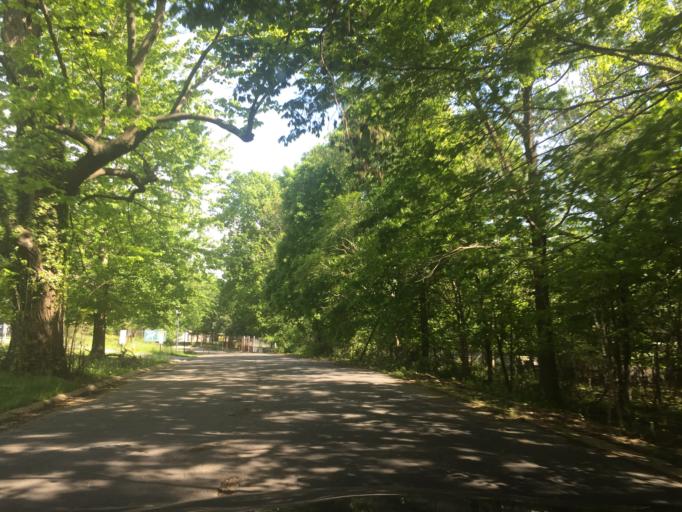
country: US
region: Maryland
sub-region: City of Baltimore
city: Baltimore
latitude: 39.3228
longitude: -76.6428
